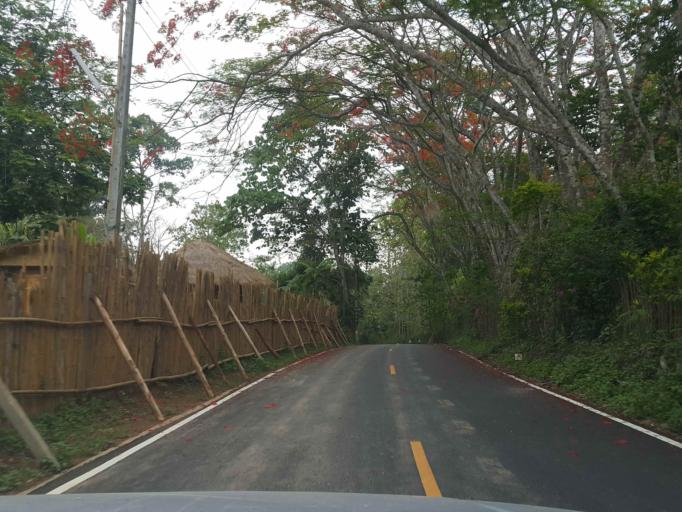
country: TH
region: Chiang Mai
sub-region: Amphoe Chiang Dao
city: Chiang Dao
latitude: 19.4095
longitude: 98.9232
